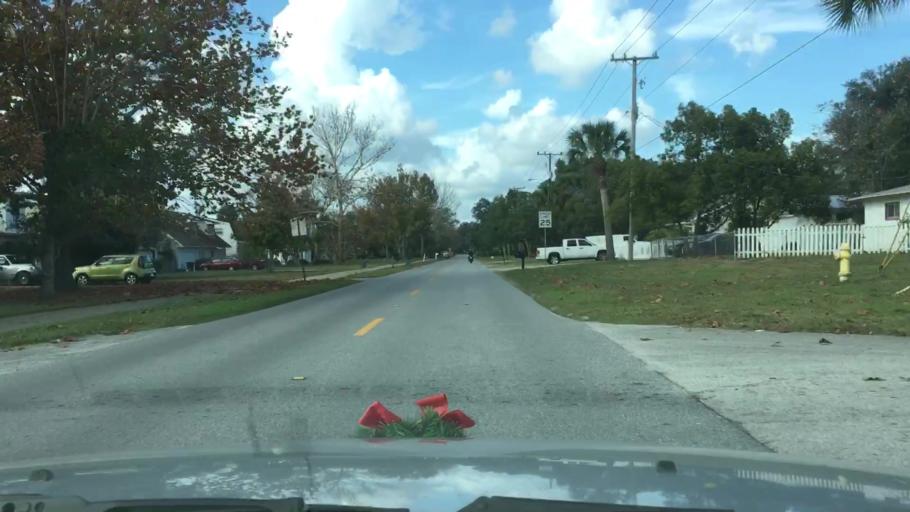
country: US
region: Florida
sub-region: Volusia County
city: Ormond Beach
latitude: 29.2942
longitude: -81.0681
